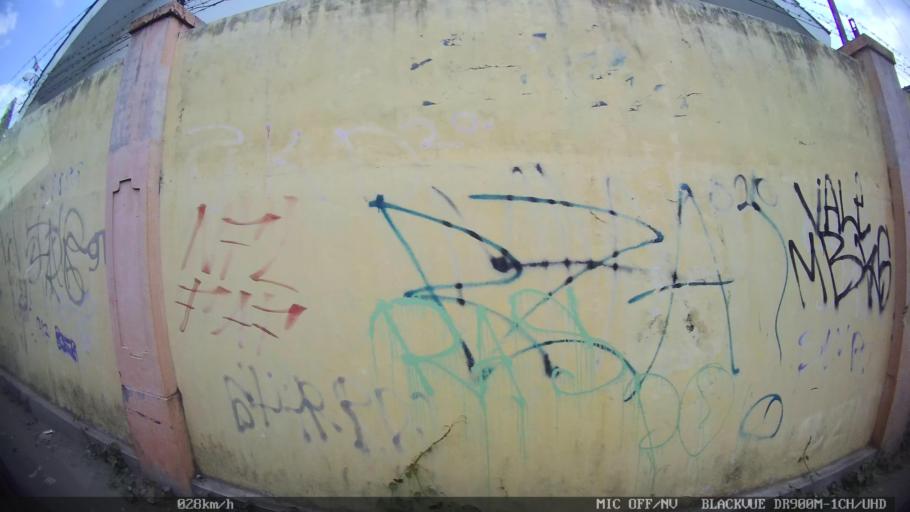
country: ID
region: Daerah Istimewa Yogyakarta
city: Gamping Lor
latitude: -7.8097
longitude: 110.3442
